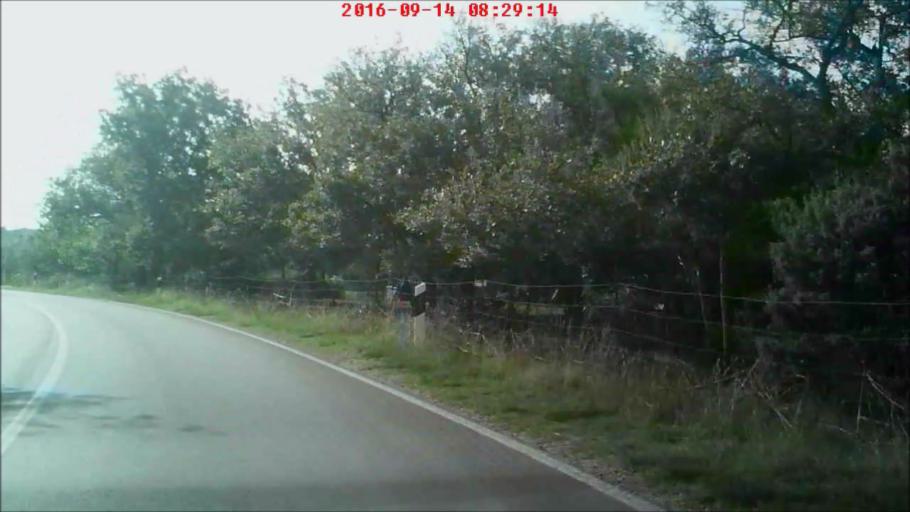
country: HR
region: Zadarska
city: Zadar
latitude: 44.1804
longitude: 15.2811
